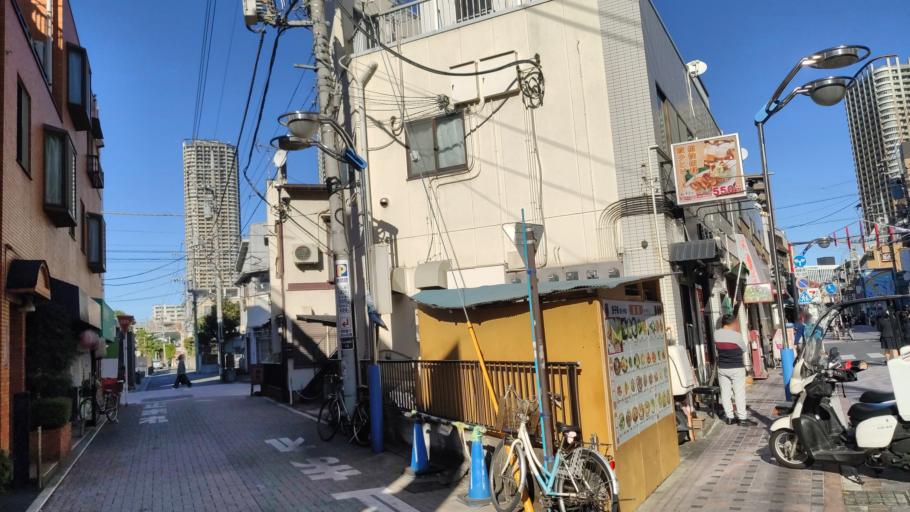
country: JP
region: Kanagawa
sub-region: Kawasaki-shi
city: Kawasaki
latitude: 35.5721
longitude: 139.6558
